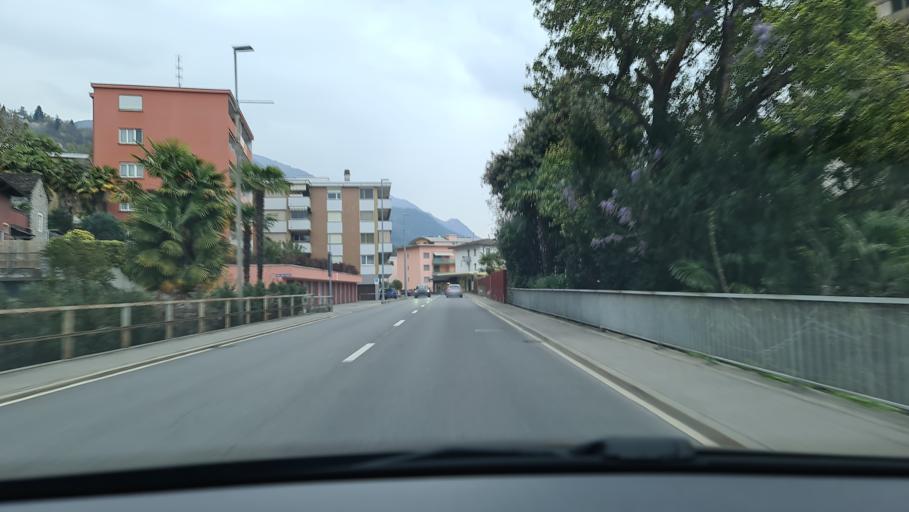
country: CH
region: Ticino
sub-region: Locarno District
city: Minusio
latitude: 46.1788
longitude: 8.8252
